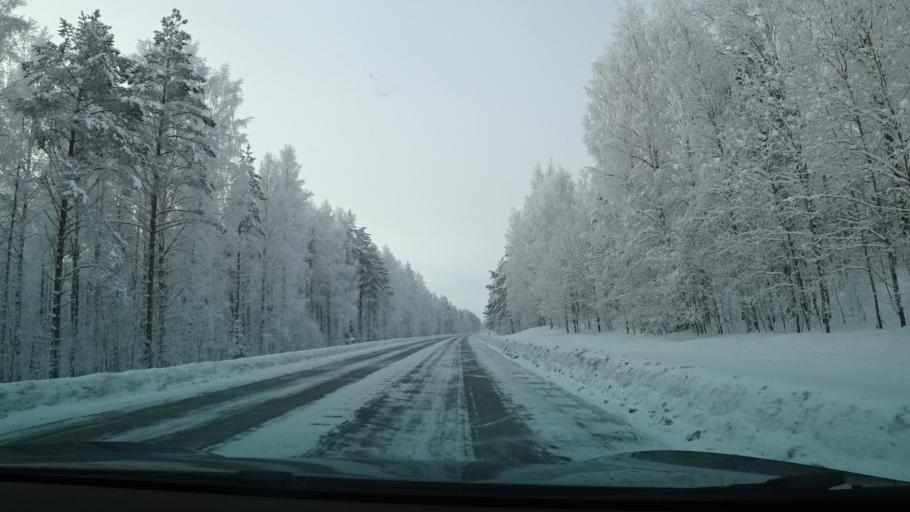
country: FI
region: South Karelia
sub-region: Imatra
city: Saari
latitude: 61.7835
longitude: 29.7129
